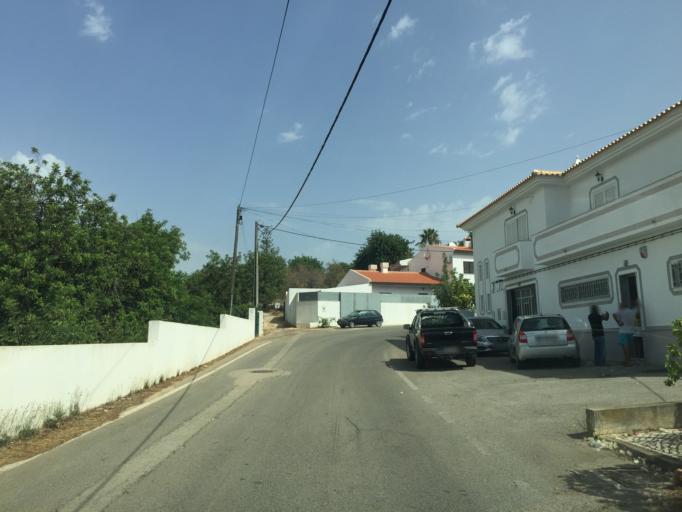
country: PT
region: Faro
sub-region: Loule
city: Boliqueime
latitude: 37.1265
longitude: -8.1428
